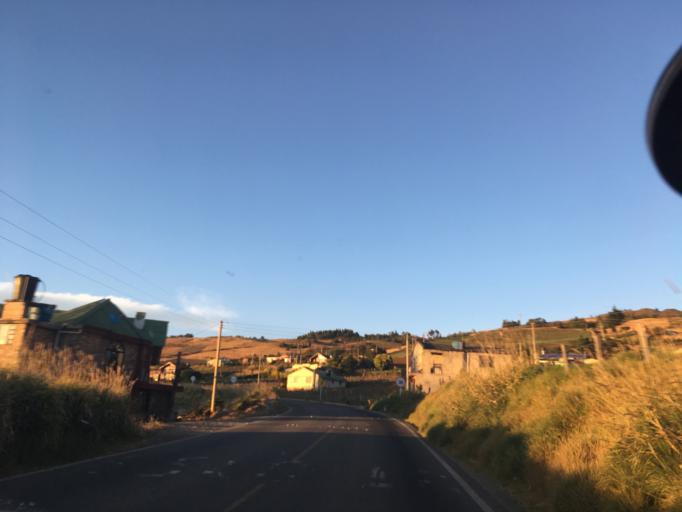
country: CO
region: Boyaca
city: Aquitania
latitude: 5.5625
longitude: -72.8834
